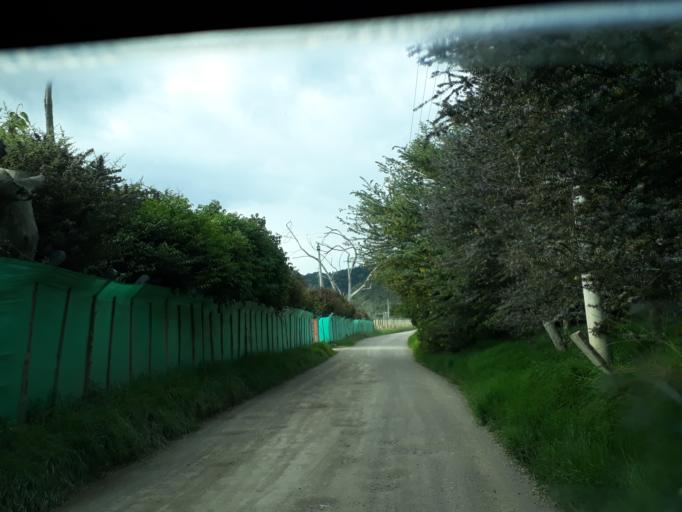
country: CO
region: Cundinamarca
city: Cucunuba
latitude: 5.2558
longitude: -73.7783
